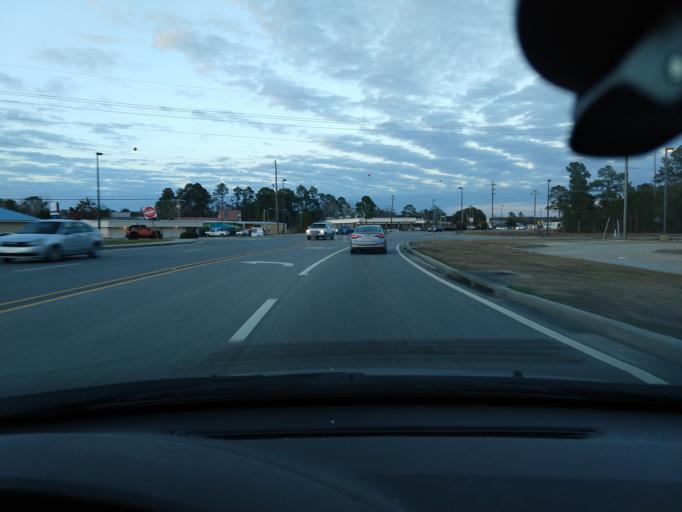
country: US
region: Mississippi
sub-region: Jackson County
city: Gulf Park Estates
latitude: 30.4133
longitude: -88.7794
